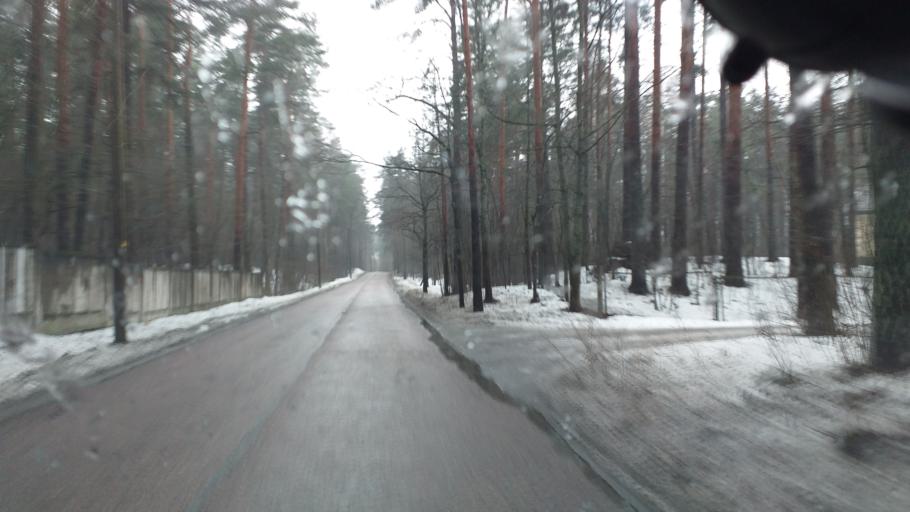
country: LV
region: Riga
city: Bolderaja
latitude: 56.9854
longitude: 24.0228
